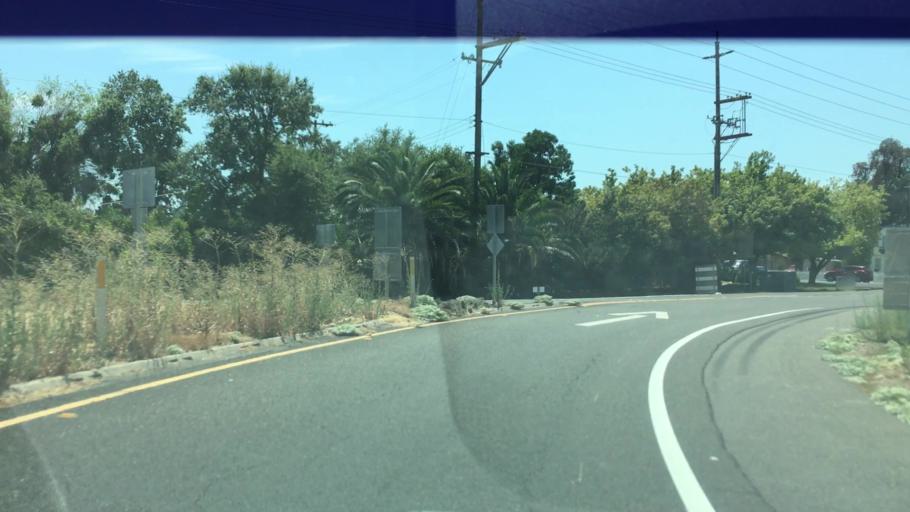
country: US
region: California
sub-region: Sacramento County
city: Galt
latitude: 38.2622
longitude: -121.2995
